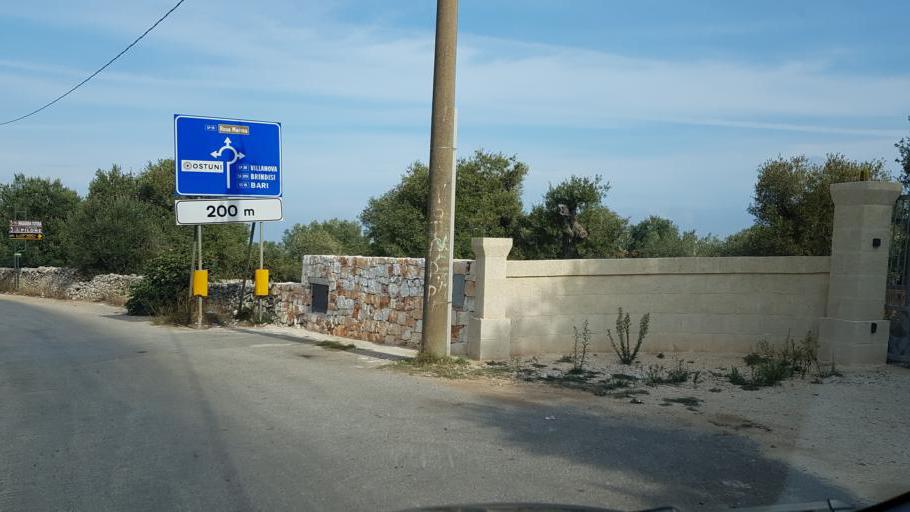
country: IT
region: Apulia
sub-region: Provincia di Brindisi
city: Ostuni
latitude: 40.7383
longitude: 17.5795
